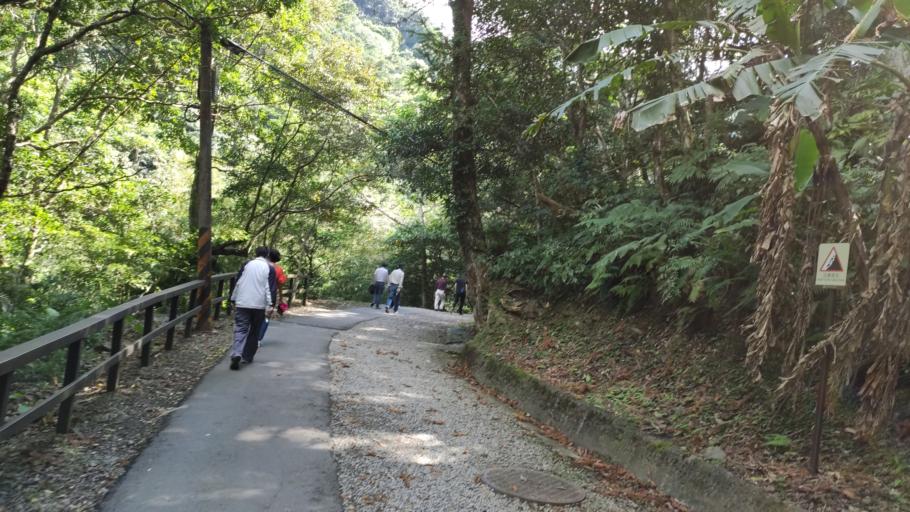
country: TW
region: Taiwan
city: Daxi
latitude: 24.8286
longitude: 121.4455
